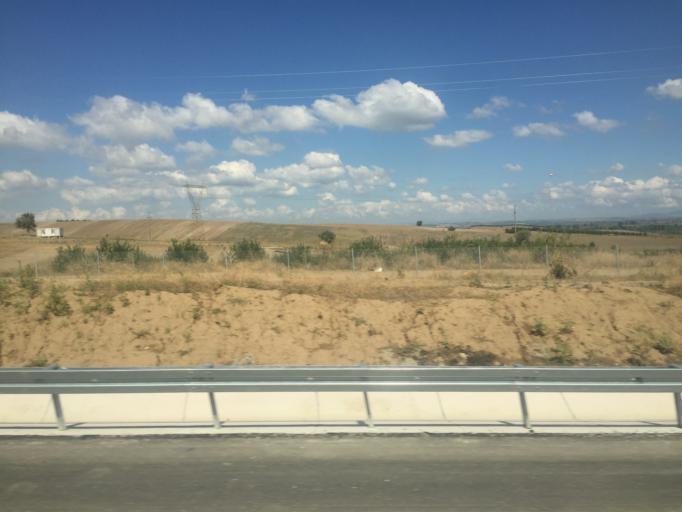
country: TR
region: Balikesir
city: Gobel
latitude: 40.0465
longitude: 28.2261
